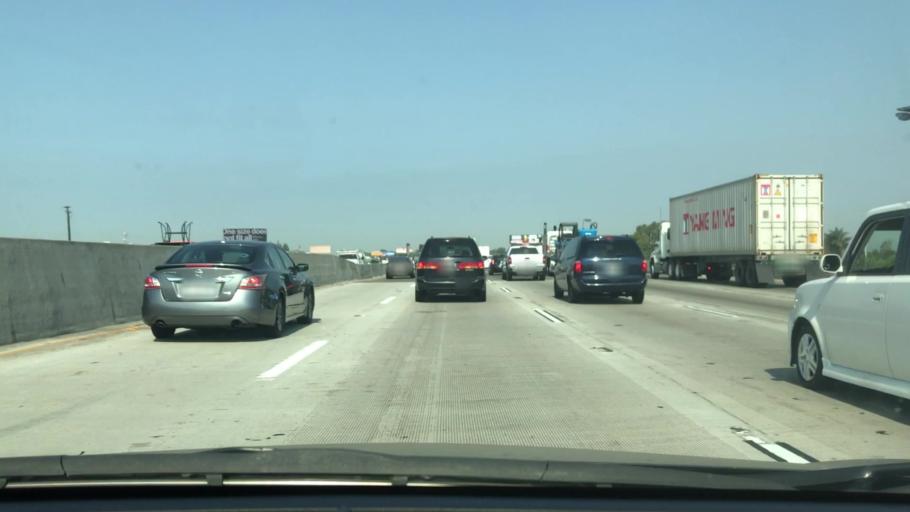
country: US
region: California
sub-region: Los Angeles County
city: Compton
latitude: 33.8743
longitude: -118.2213
